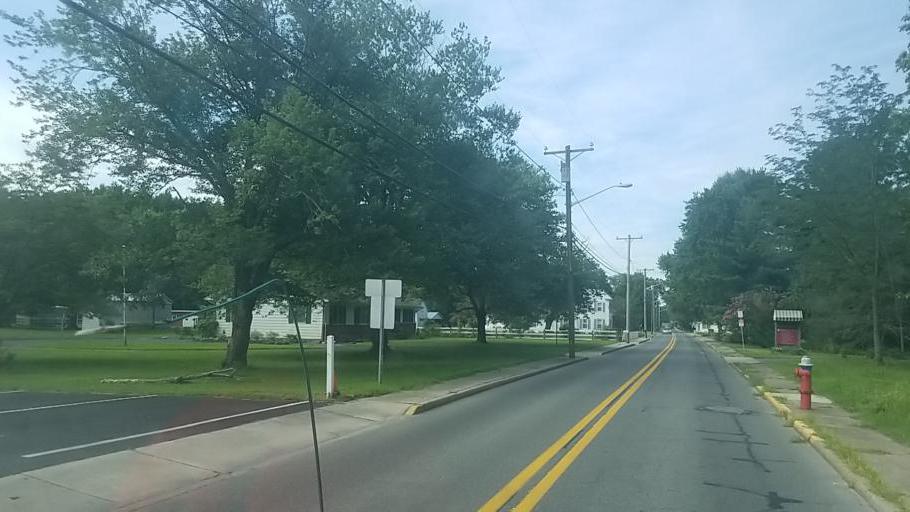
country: US
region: Delaware
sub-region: Sussex County
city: Selbyville
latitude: 38.5198
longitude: -75.2281
